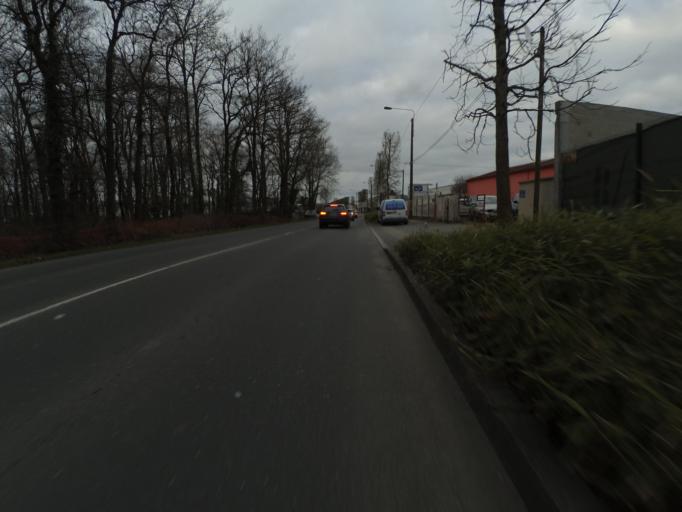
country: FR
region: Pays de la Loire
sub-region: Departement de la Loire-Atlantique
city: Sainte-Luce-sur-Loire
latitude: 47.2714
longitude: -1.5000
